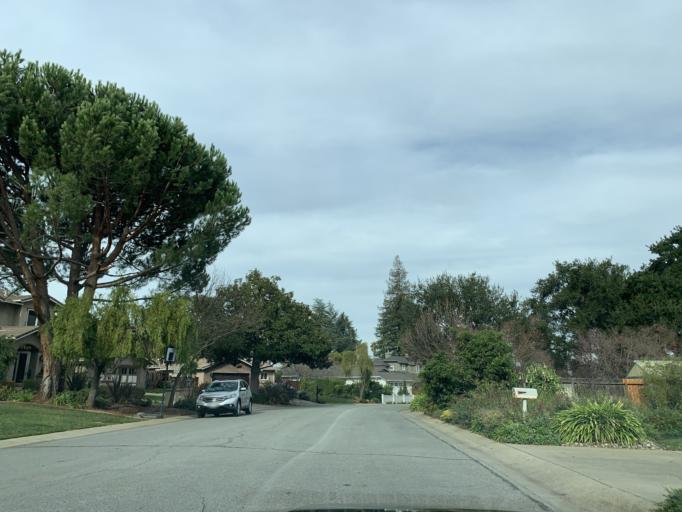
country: US
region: California
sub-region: Santa Clara County
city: Los Altos
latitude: 37.3778
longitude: -122.1029
